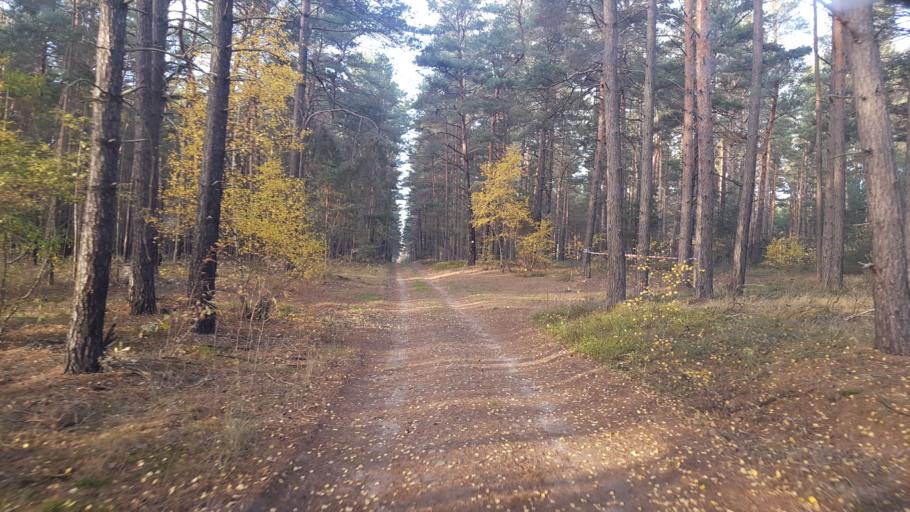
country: DE
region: Brandenburg
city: Calau
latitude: 51.7001
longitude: 13.9561
